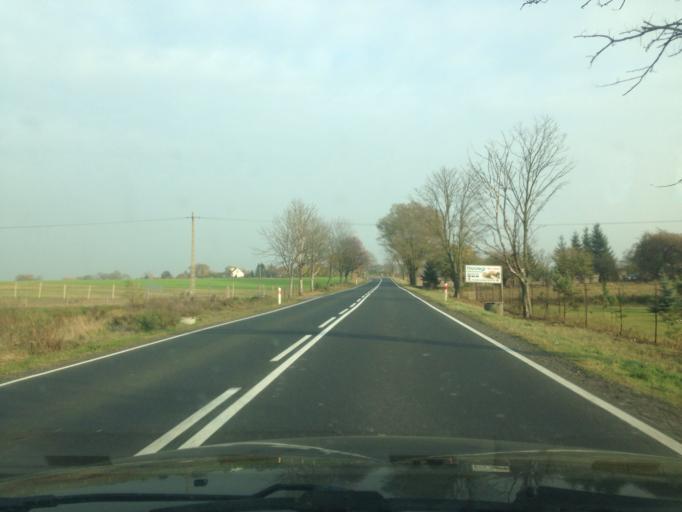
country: PL
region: Kujawsko-Pomorskie
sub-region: Powiat brodnicki
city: Bobrowo
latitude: 53.2348
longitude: 19.2710
